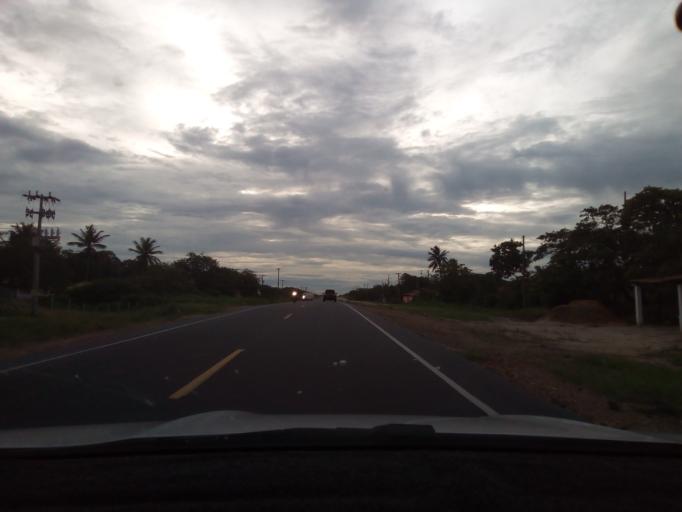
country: BR
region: Ceara
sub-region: Aracati
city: Aracati
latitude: -4.3686
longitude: -37.9432
